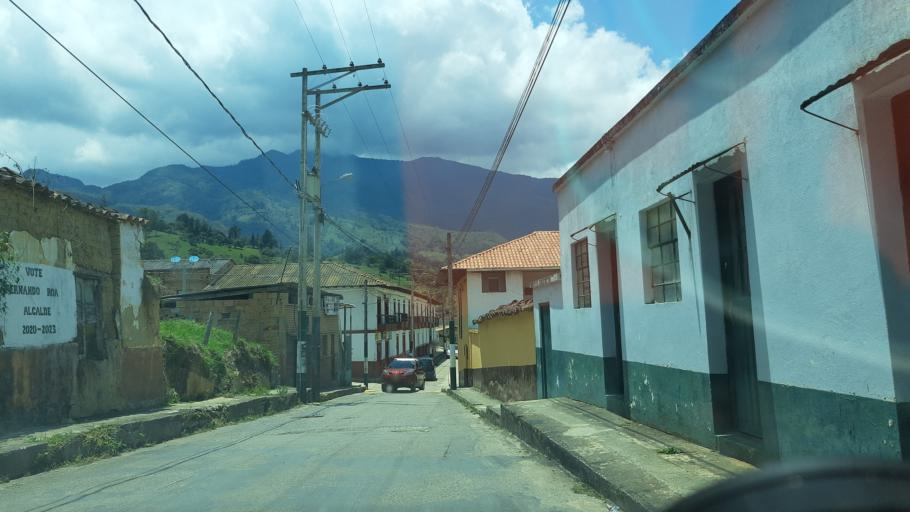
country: CO
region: Boyaca
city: Chinavita
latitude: 5.1385
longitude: -73.3962
